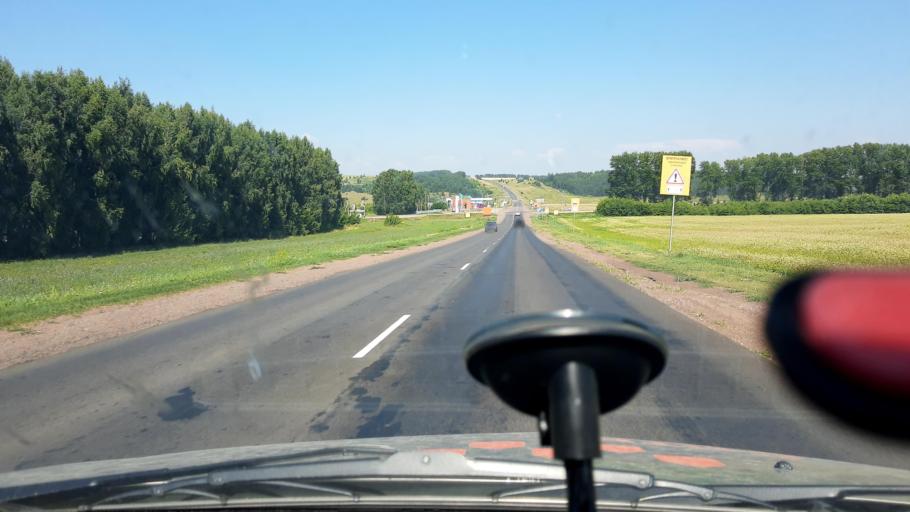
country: RU
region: Bashkortostan
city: Chekmagush
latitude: 55.1280
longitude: 54.6807
